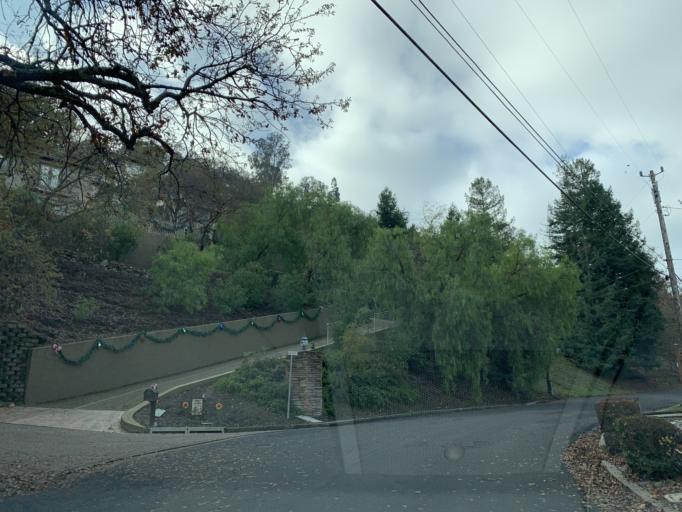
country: US
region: California
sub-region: Contra Costa County
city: Saranap
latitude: 37.8852
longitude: -122.0711
